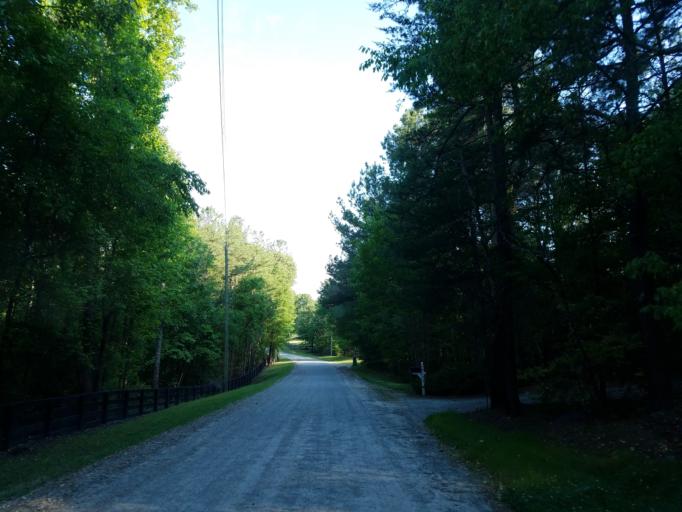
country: US
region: Georgia
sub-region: Pickens County
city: Nelson
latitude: 34.3696
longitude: -84.3275
